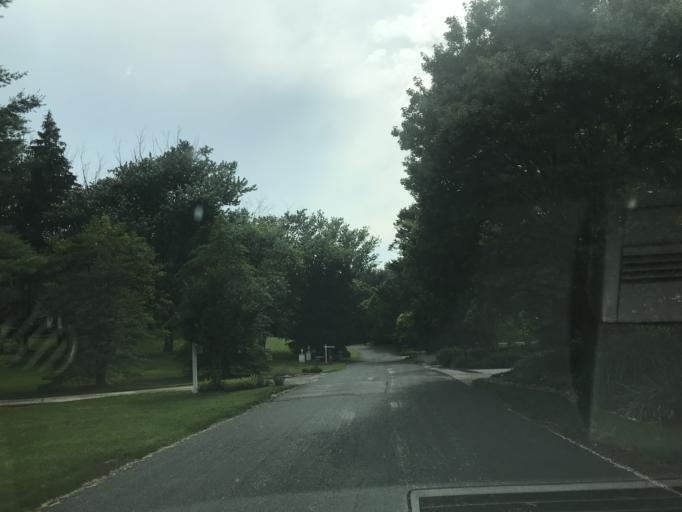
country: US
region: Maryland
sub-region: Baltimore County
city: Hampton
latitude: 39.4220
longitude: -76.5924
